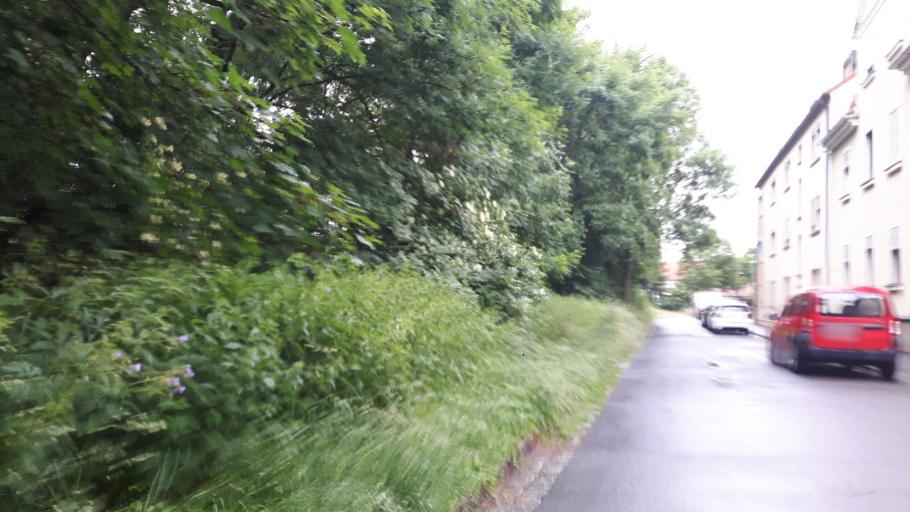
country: DE
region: Bavaria
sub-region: Regierungsbezirk Unterfranken
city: Schweinfurt
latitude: 50.0565
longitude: 10.2322
